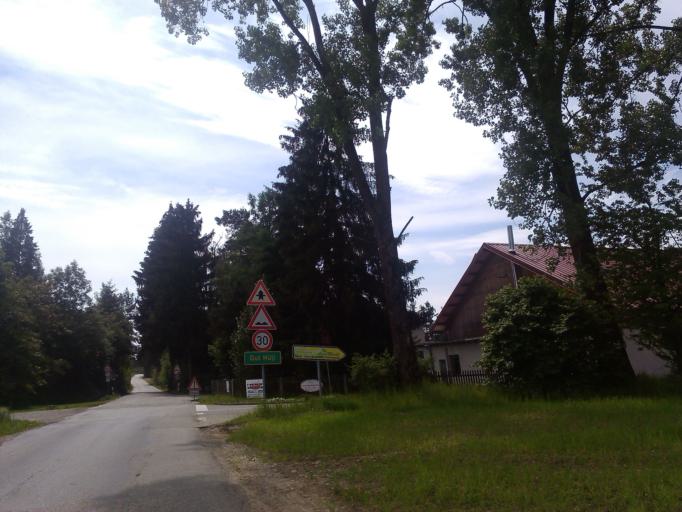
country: DE
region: Bavaria
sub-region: Upper Bavaria
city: Gilching
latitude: 48.0949
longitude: 11.3231
